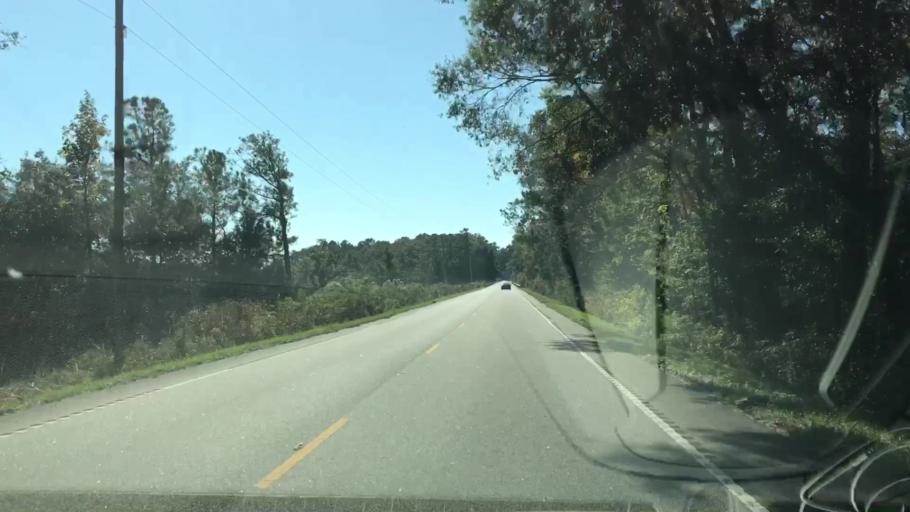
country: US
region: South Carolina
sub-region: Jasper County
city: Ridgeland
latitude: 32.5539
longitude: -80.9134
